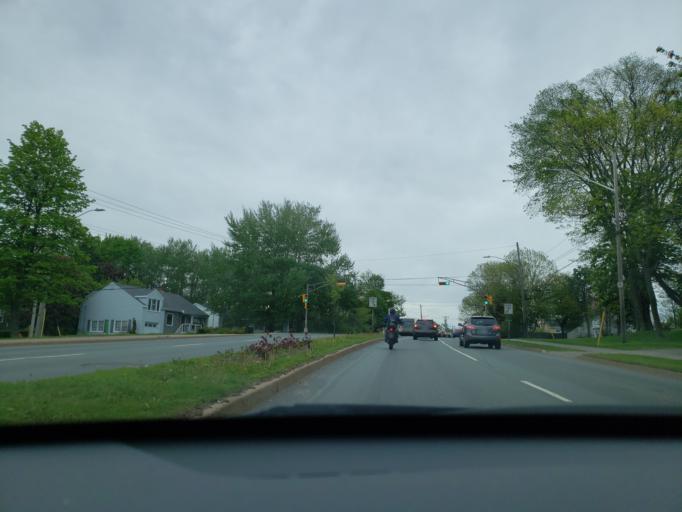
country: CA
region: Nova Scotia
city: Dartmouth
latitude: 44.6836
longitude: -63.5333
